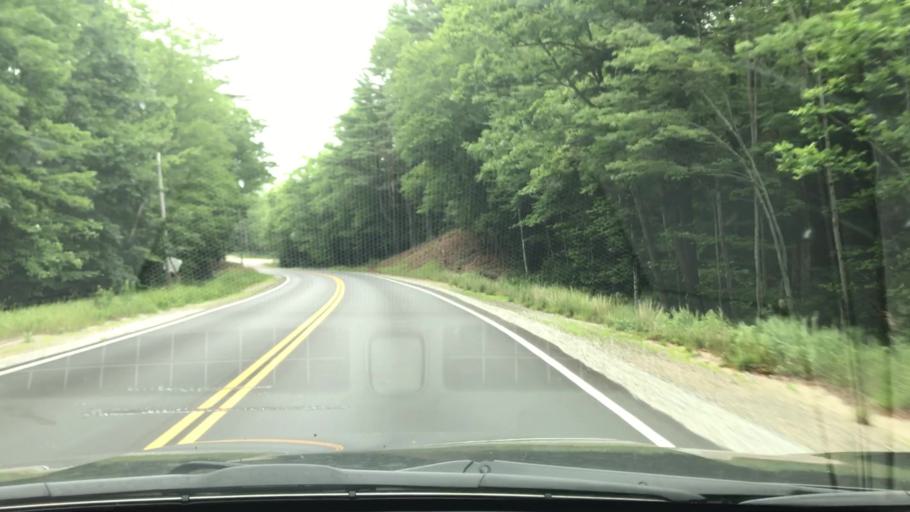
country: US
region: Maine
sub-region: Oxford County
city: West Paris
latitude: 44.3942
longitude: -70.6630
